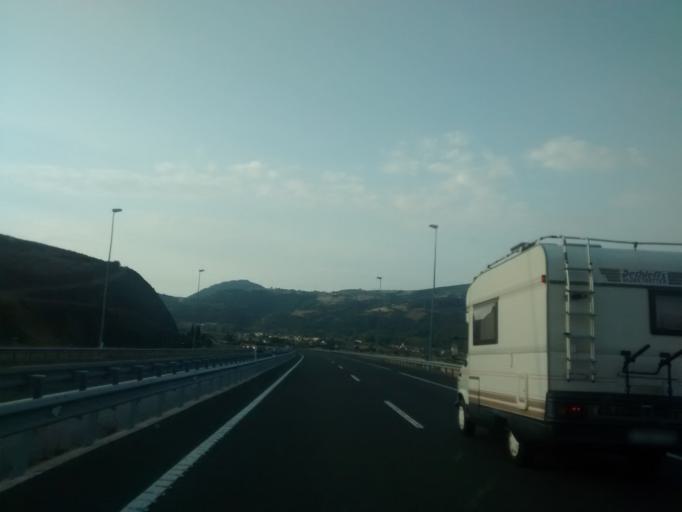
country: ES
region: Cantabria
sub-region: Provincia de Cantabria
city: Molledo
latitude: 43.1641
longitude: -4.0527
